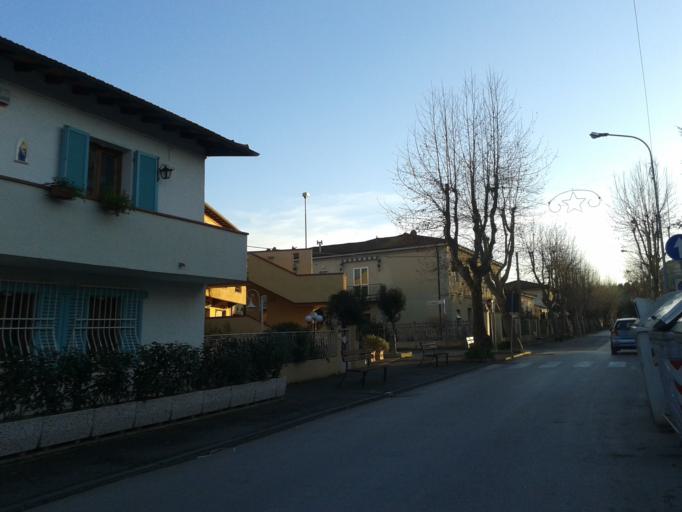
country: IT
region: Tuscany
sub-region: Provincia di Livorno
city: Guasticce
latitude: 43.5974
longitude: 10.4067
